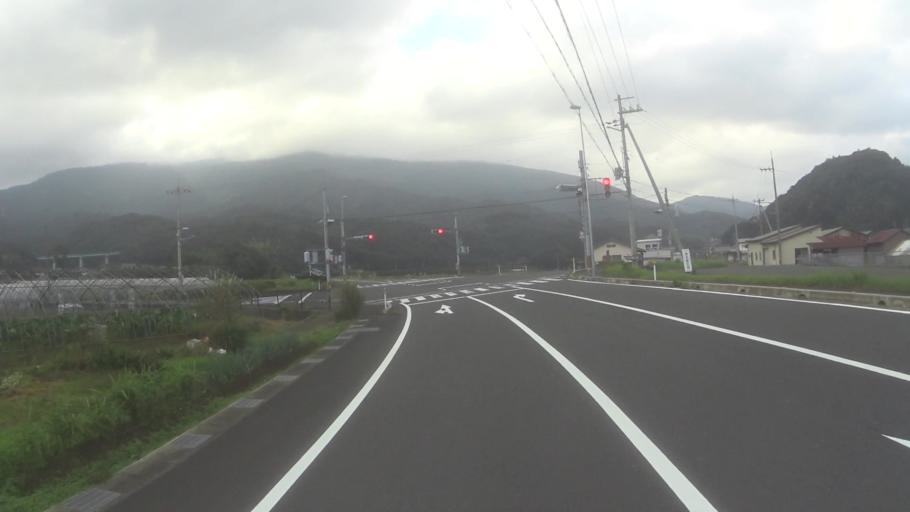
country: JP
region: Kyoto
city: Miyazu
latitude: 35.5136
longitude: 135.1861
